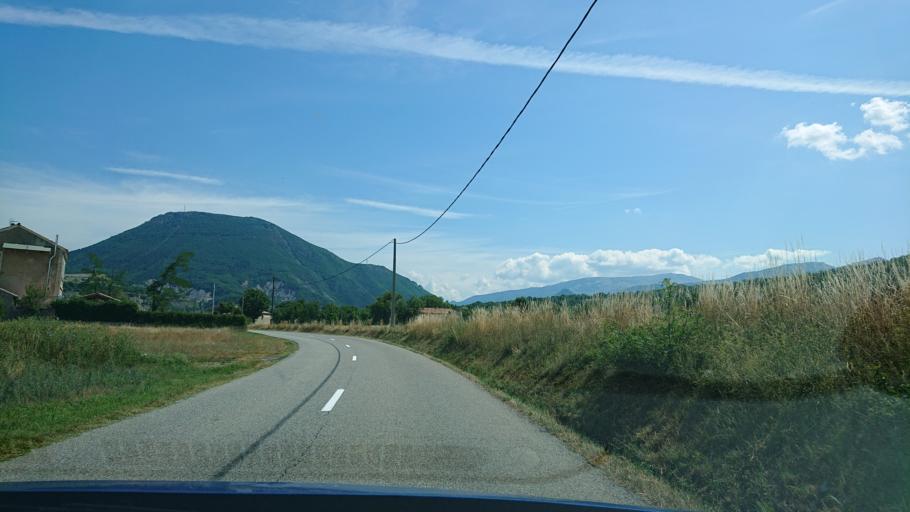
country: FR
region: Provence-Alpes-Cote d'Azur
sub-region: Departement des Alpes-de-Haute-Provence
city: Sisteron
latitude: 44.2514
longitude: 5.9592
